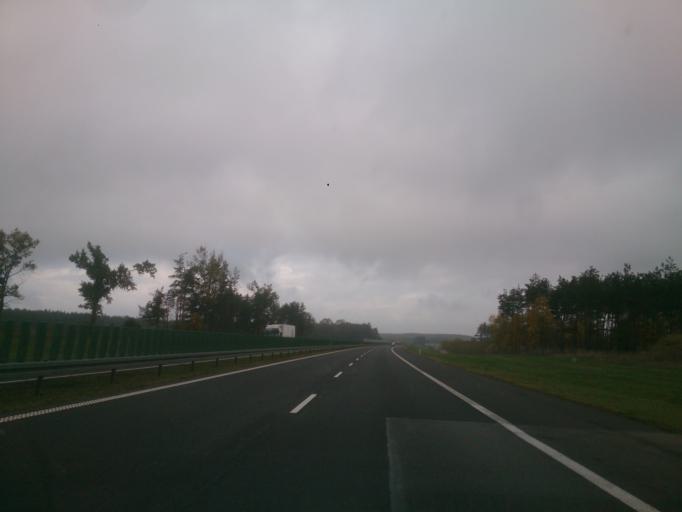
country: PL
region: Pomeranian Voivodeship
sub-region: Powiat starogardzki
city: Smetowo Graniczne
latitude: 53.8007
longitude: 18.6249
